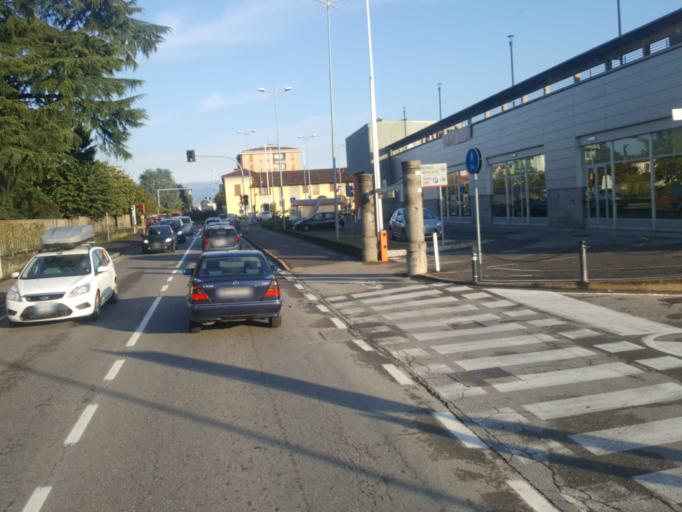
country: IT
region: Lombardy
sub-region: Provincia di Bergamo
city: Urgnano
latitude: 45.5970
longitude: 9.7001
